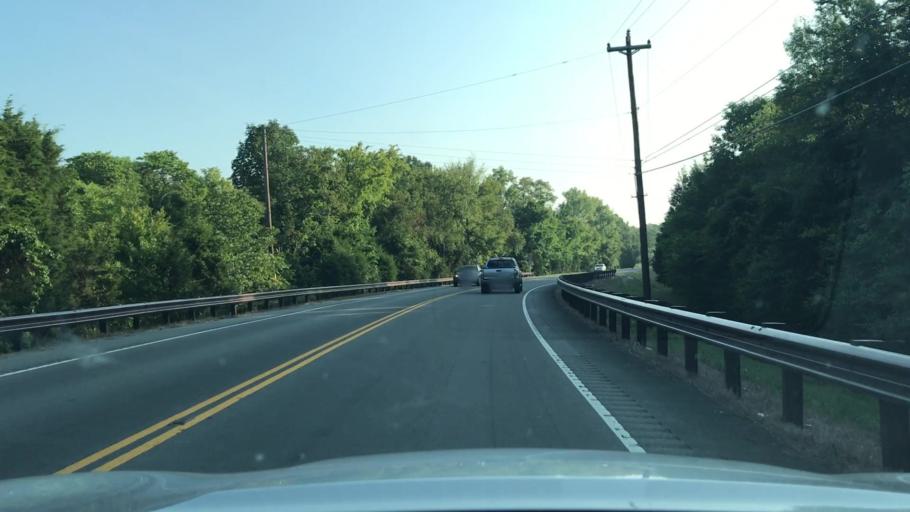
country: US
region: Tennessee
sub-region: Wilson County
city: Rural Hill
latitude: 36.1051
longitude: -86.5513
